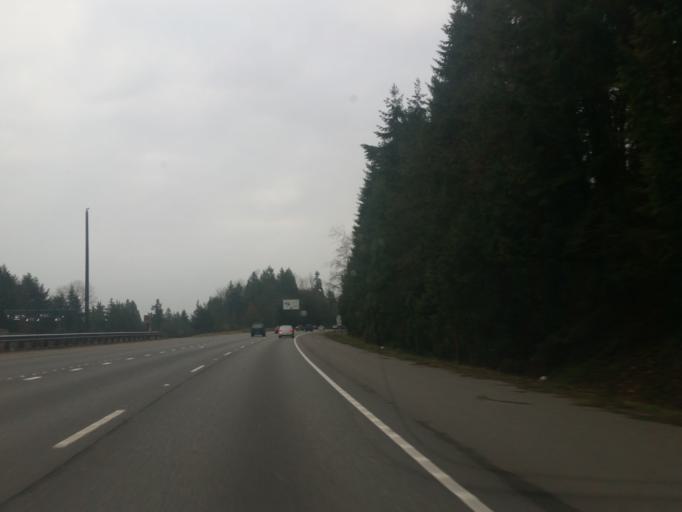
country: US
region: Washington
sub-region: King County
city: Bothell
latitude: 47.7880
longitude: -122.2012
